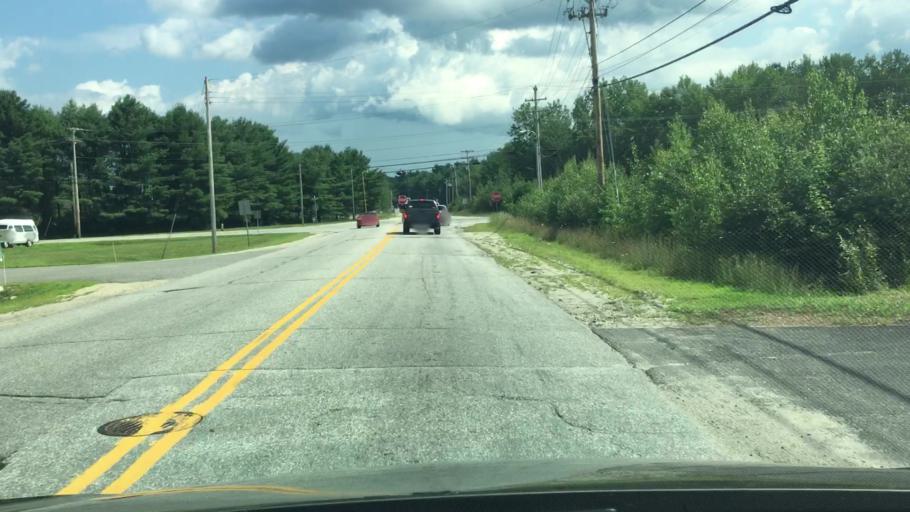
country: US
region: Maine
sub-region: Androscoggin County
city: Auburn
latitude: 44.0749
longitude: -70.2557
